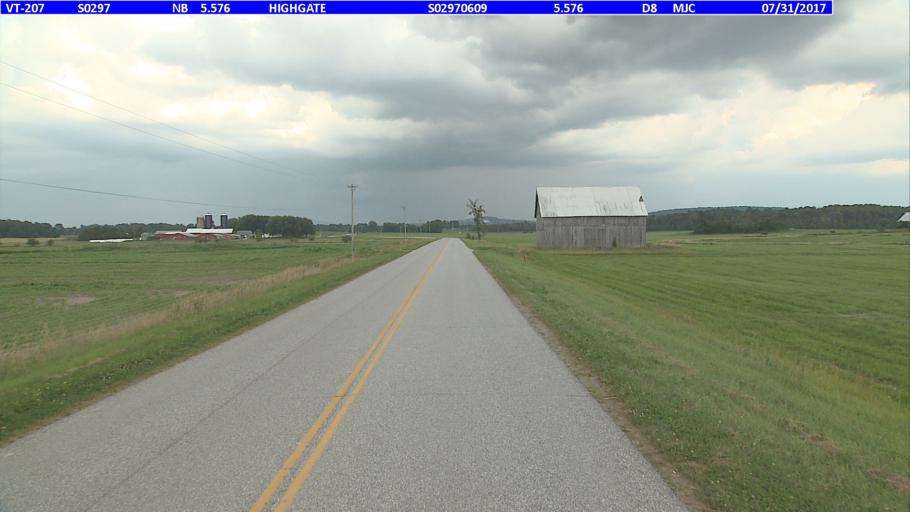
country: CA
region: Quebec
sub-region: Monteregie
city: Bedford
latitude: 45.0054
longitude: -72.9950
